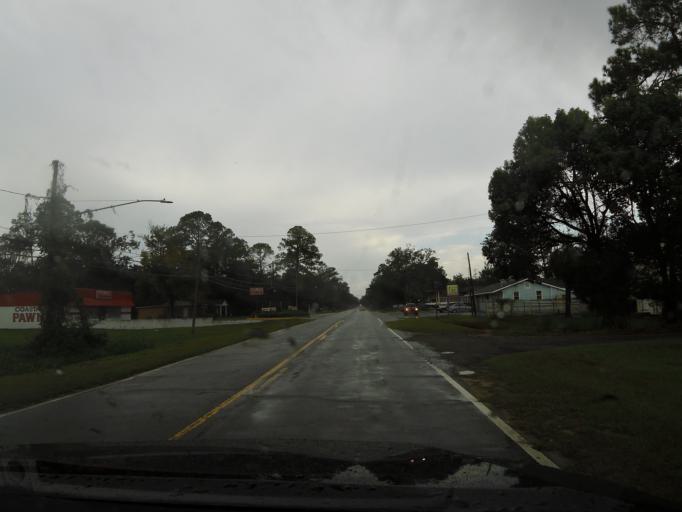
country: US
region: Georgia
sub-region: Wayne County
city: Jesup
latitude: 31.5976
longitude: -81.8738
